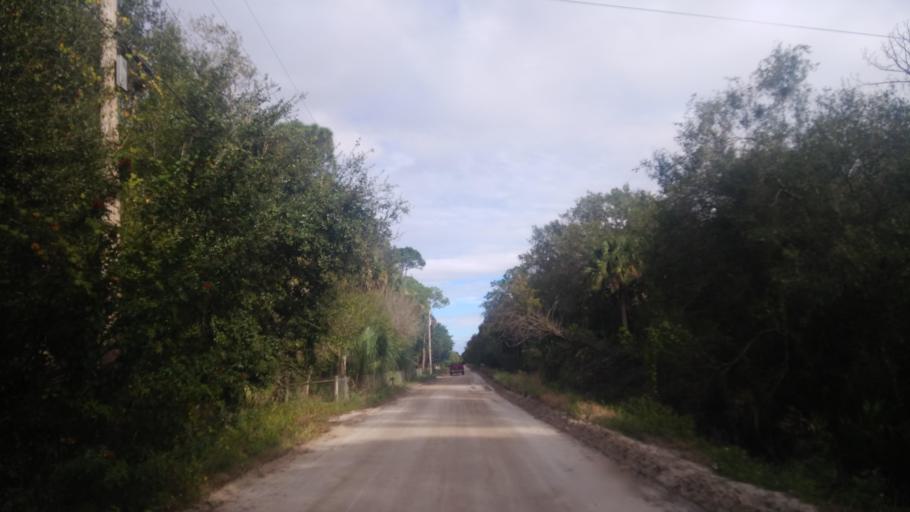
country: US
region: Florida
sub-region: Indian River County
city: Fellsmere
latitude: 27.7610
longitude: -80.5871
